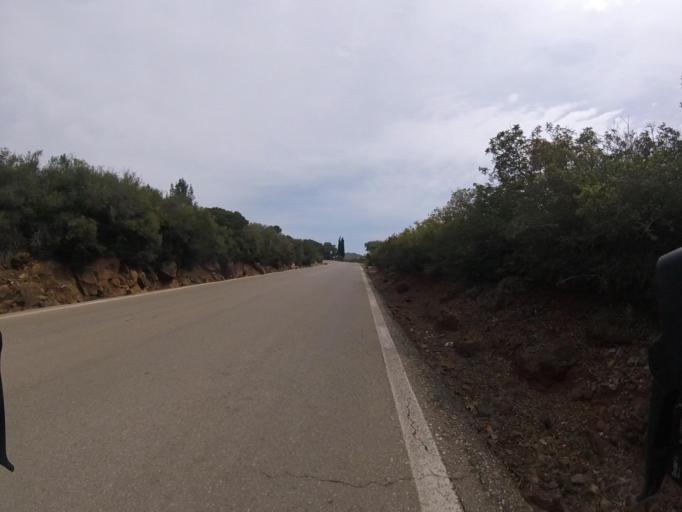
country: ES
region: Valencia
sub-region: Provincia de Castello
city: Cabanes
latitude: 40.1562
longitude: 0.0620
